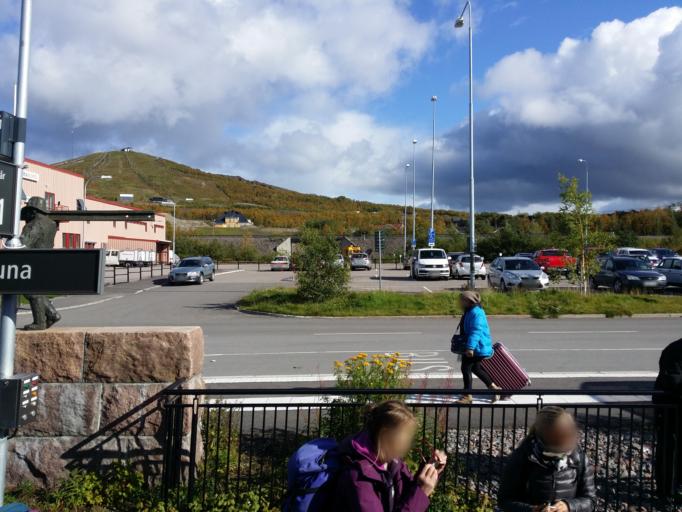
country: SE
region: Norrbotten
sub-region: Kiruna Kommun
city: Kiruna
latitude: 67.8680
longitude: 20.1999
